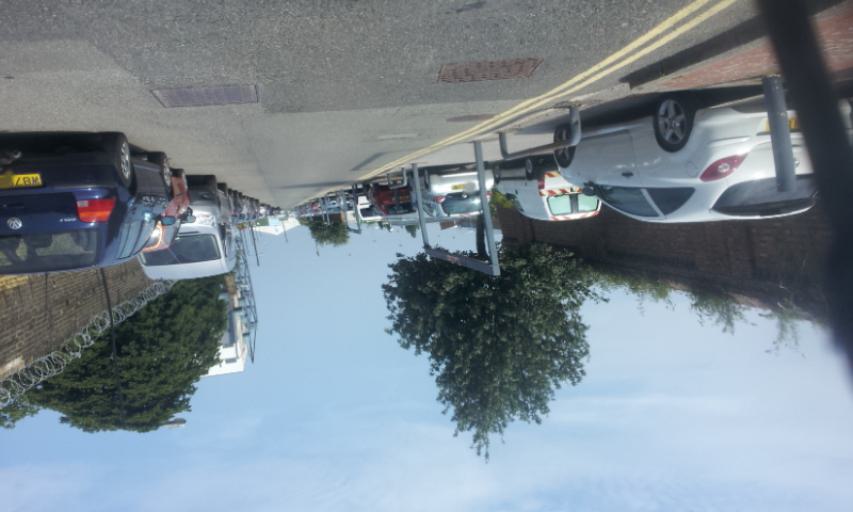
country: GB
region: England
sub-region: Kent
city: Gillingham
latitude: 51.3960
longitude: 0.5524
